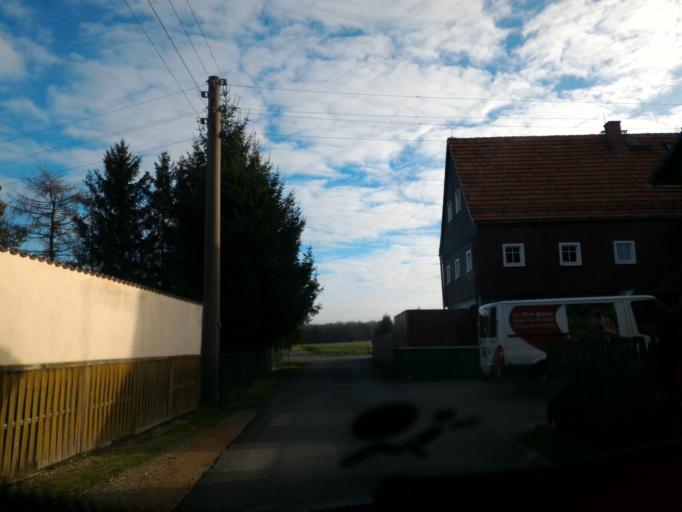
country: DE
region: Saxony
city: Grossschonau
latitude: 50.8735
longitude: 14.6535
